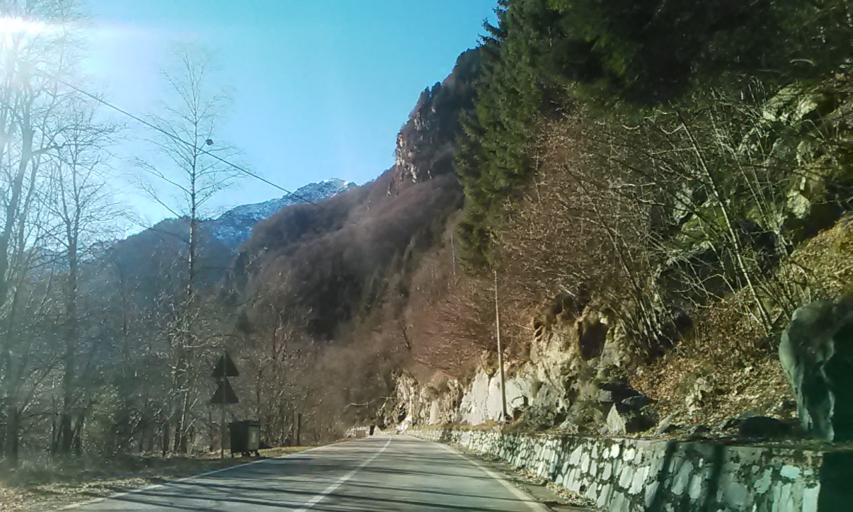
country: IT
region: Piedmont
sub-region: Provincia di Vercelli
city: Rimasco
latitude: 45.8731
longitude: 8.0700
